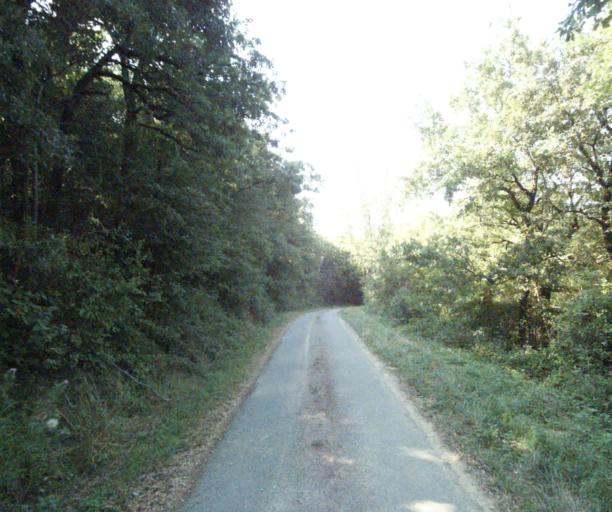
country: FR
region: Midi-Pyrenees
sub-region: Departement de la Haute-Garonne
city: Saint-Felix-Lauragais
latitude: 43.4292
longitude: 1.8284
